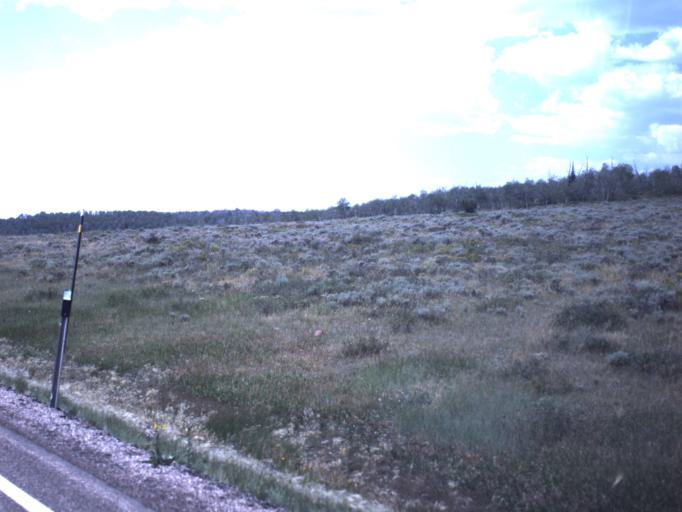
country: US
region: Utah
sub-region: Uintah County
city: Maeser
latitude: 40.6922
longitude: -109.4944
